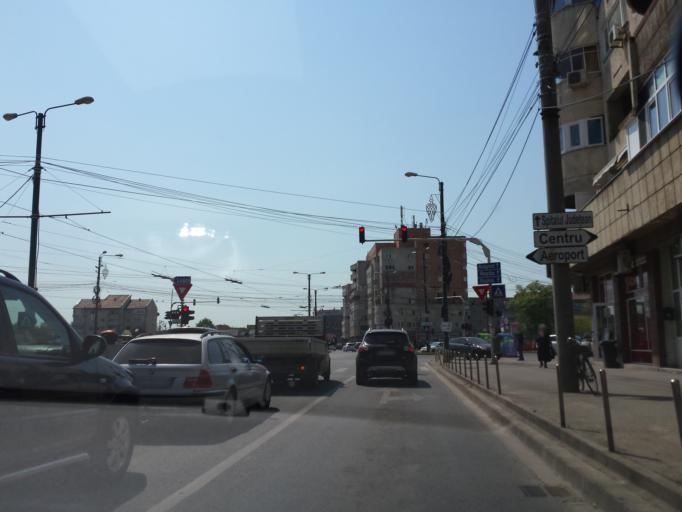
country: RO
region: Timis
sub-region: Comuna Dumbravita
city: Dumbravita
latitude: 45.7660
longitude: 21.2604
